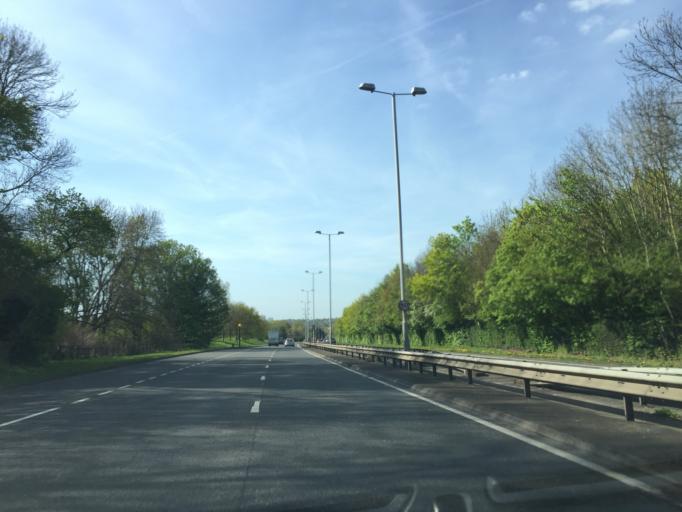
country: GB
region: England
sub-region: Greater London
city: Sidcup
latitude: 51.4241
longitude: 0.0894
